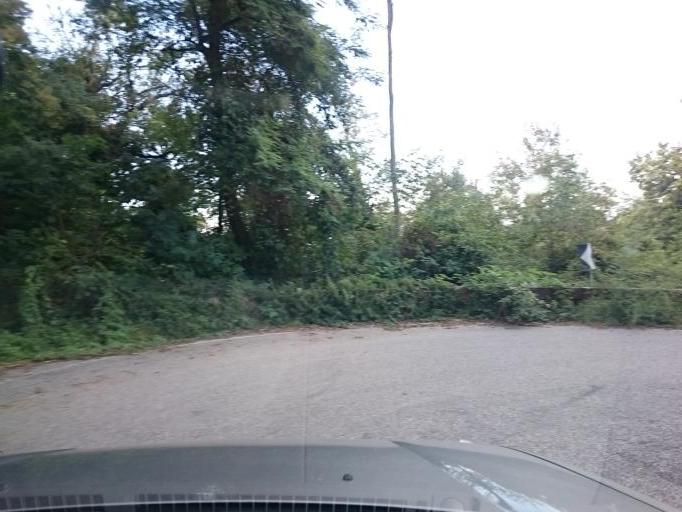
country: IT
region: Veneto
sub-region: Provincia di Padova
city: Galzignano
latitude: 45.3194
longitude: 11.7012
